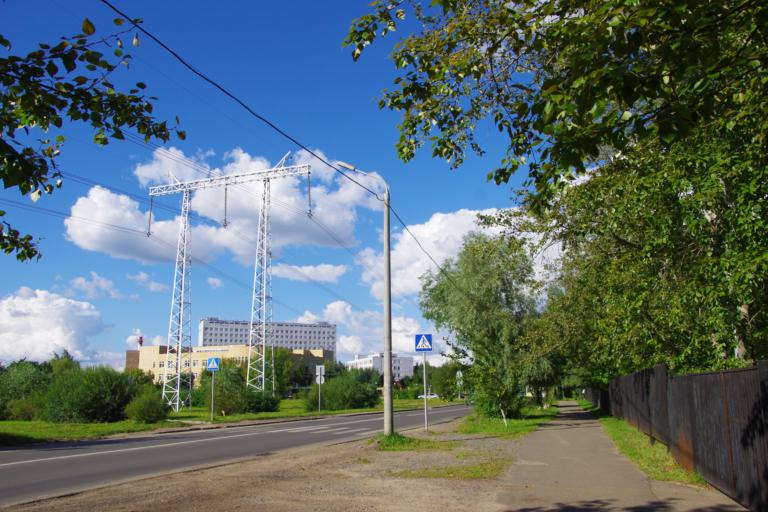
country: RU
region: Moskovskaya
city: Krasnogorsk
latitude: 55.8331
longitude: 37.3075
